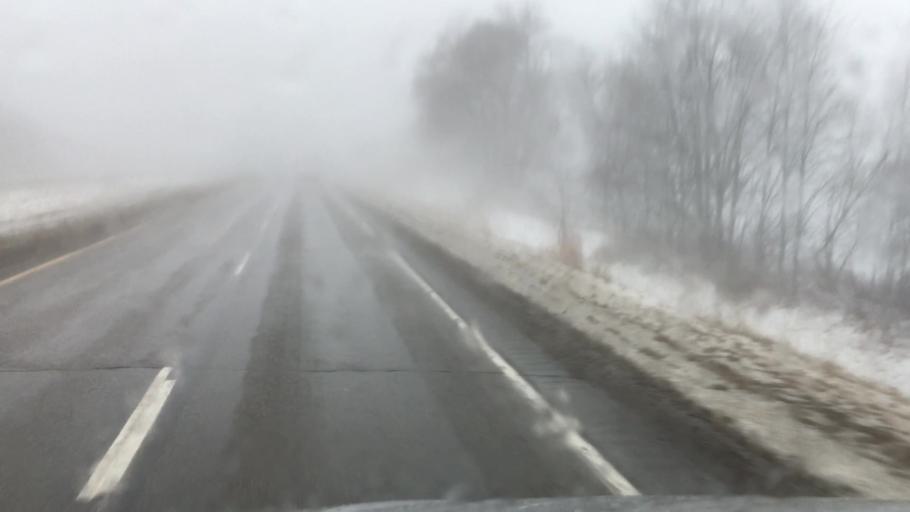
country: US
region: Indiana
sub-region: Newton County
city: Roselawn
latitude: 41.1275
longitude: -87.4523
